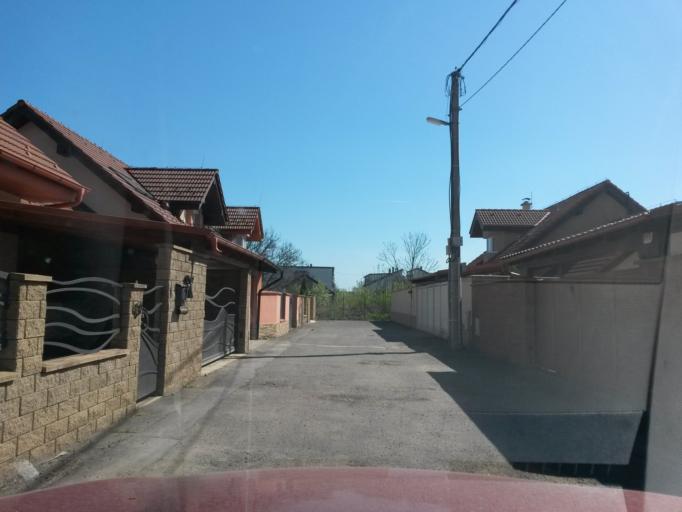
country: SK
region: Kosicky
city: Kosice
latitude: 48.6806
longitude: 21.2747
